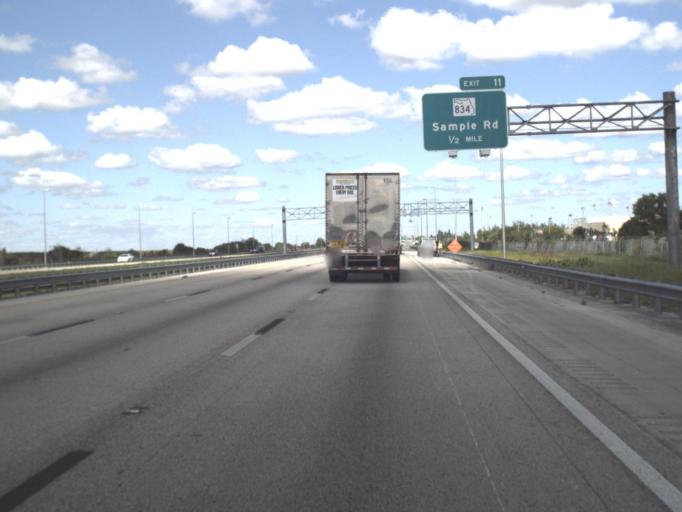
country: US
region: Florida
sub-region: Broward County
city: Coral Springs
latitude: 26.2595
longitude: -80.2969
